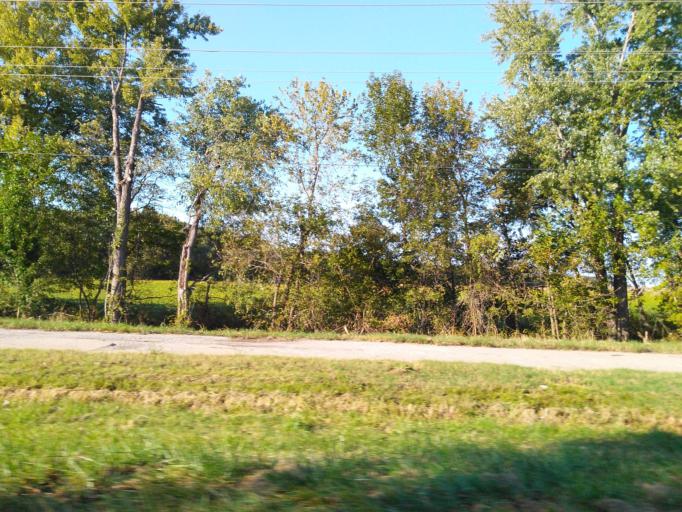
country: US
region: Illinois
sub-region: Madison County
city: Troy
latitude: 38.7162
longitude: -89.8268
